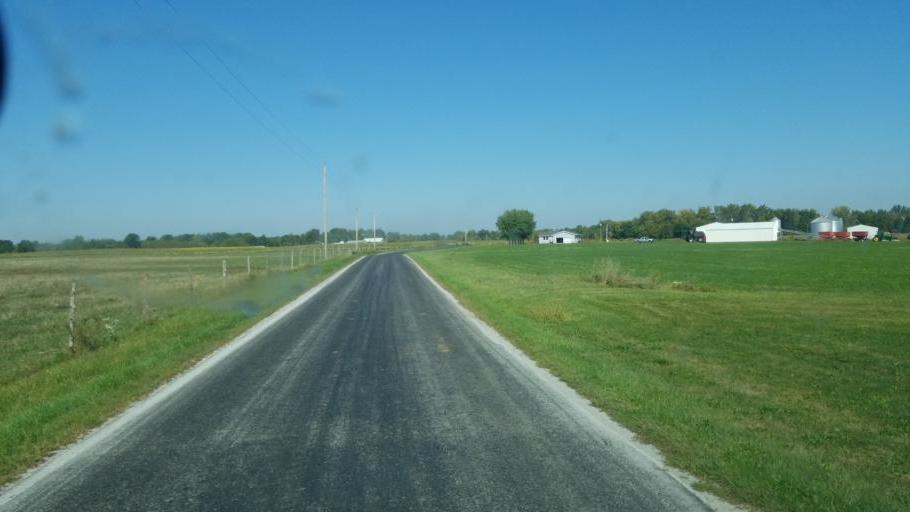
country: US
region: Ohio
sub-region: Hardin County
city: Kenton
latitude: 40.6119
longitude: -83.4918
